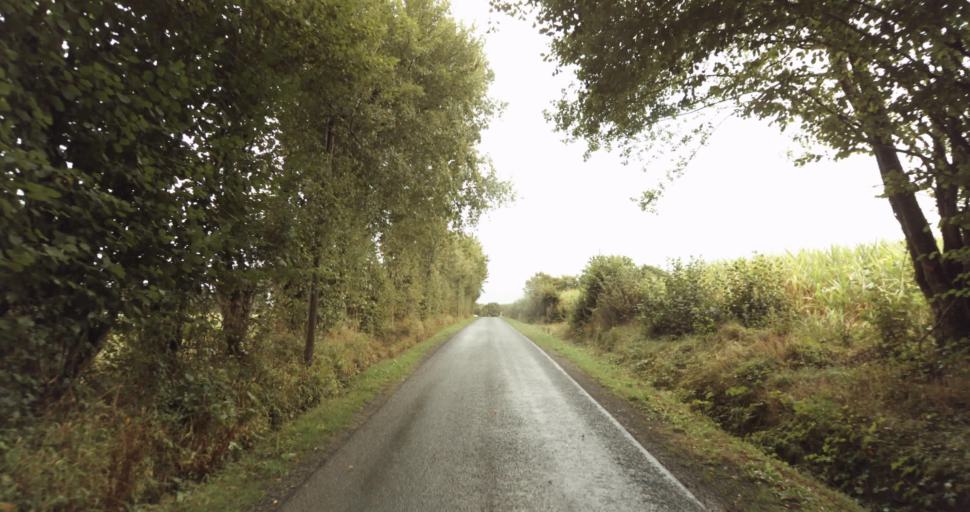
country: FR
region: Lower Normandy
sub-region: Departement de l'Orne
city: Sainte-Gauburge-Sainte-Colombe
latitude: 48.6898
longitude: 0.4144
